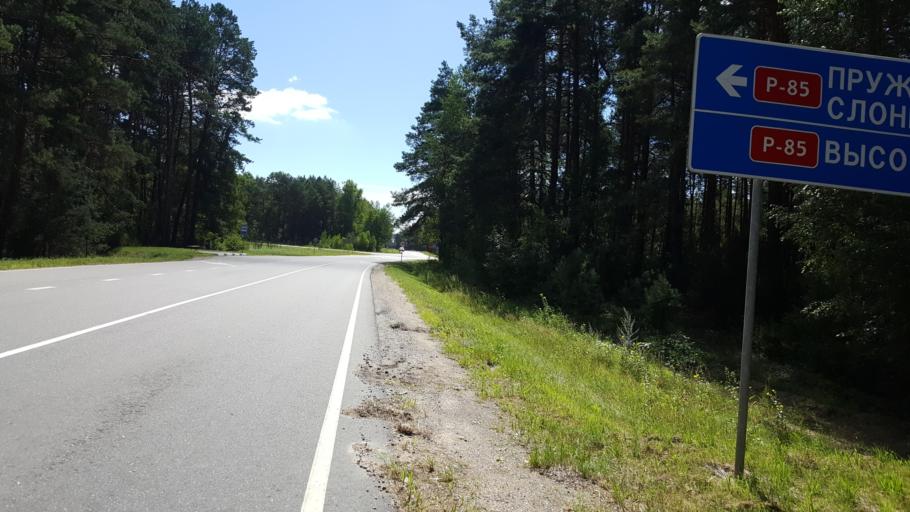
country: BY
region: Brest
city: Zhabinka
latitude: 52.3805
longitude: 24.1206
